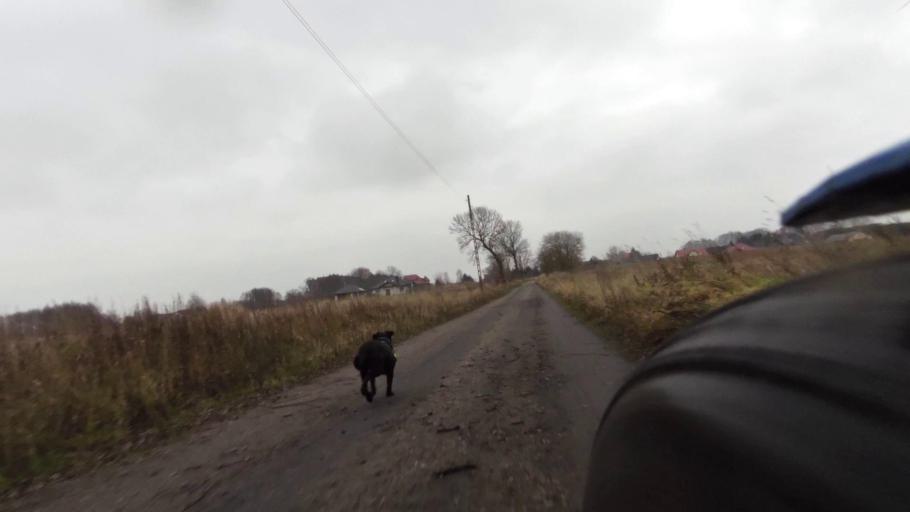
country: PL
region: West Pomeranian Voivodeship
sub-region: Powiat szczecinecki
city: Szczecinek
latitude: 53.6635
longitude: 16.6665
